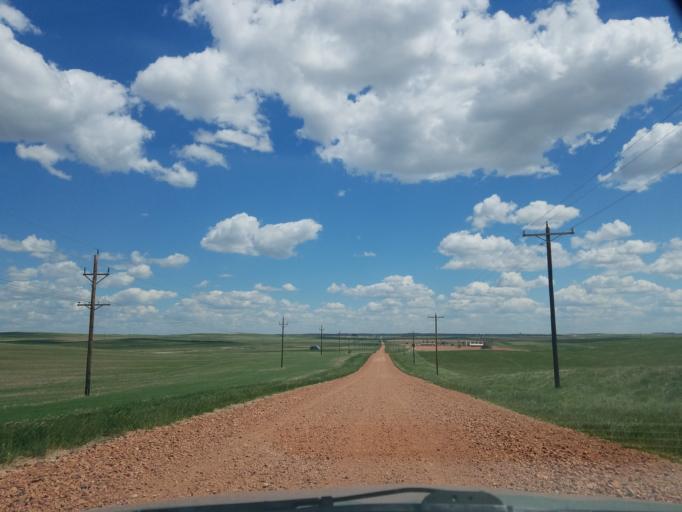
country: US
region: North Dakota
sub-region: McKenzie County
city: Watford City
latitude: 47.8194
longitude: -103.6039
